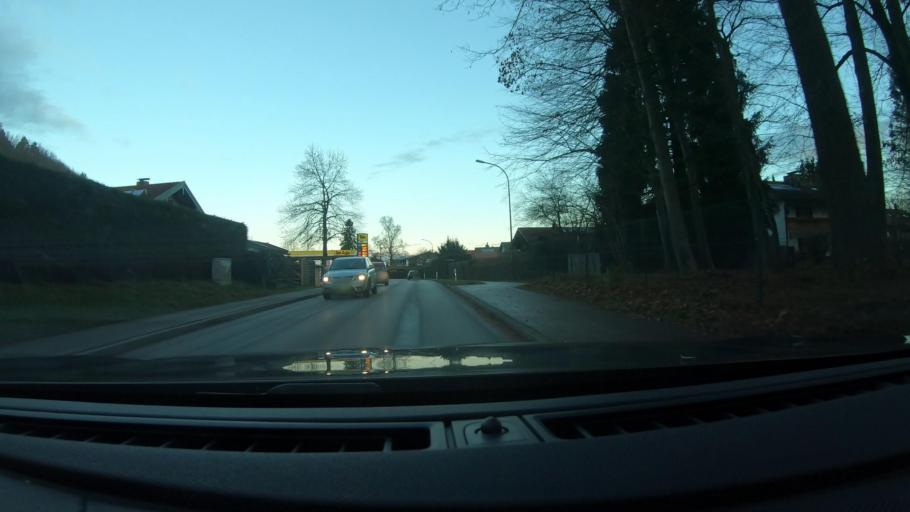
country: DE
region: Bavaria
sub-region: Upper Bavaria
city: Siegsdorf
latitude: 47.8231
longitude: 12.6394
